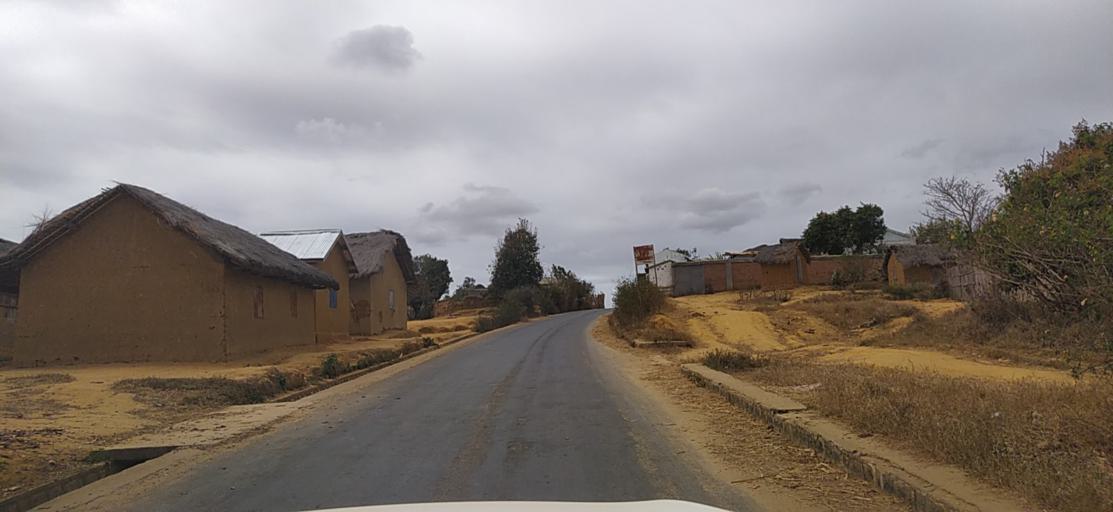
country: MG
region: Alaotra Mangoro
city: Ambatondrazaka
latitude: -17.9299
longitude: 48.2564
